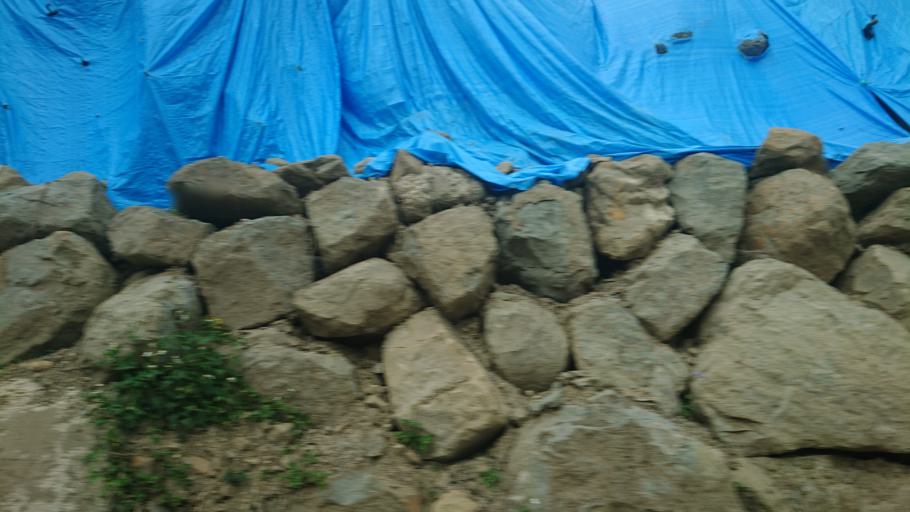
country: TW
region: Taiwan
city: Lugu
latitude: 23.6001
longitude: 120.6984
